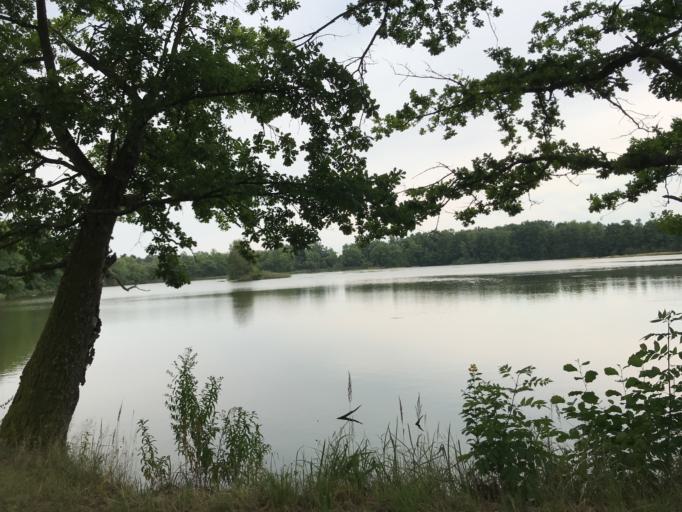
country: CZ
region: Jihocesky
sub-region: Okres Jindrichuv Hradec
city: Trebon
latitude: 48.9851
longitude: 14.7871
